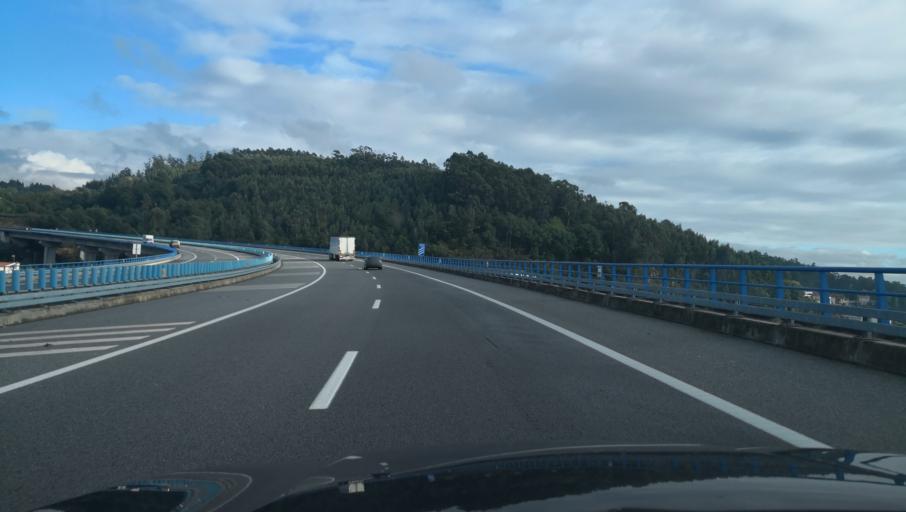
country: PT
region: Braga
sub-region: Guimaraes
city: Candoso
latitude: 41.4099
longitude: -8.3223
